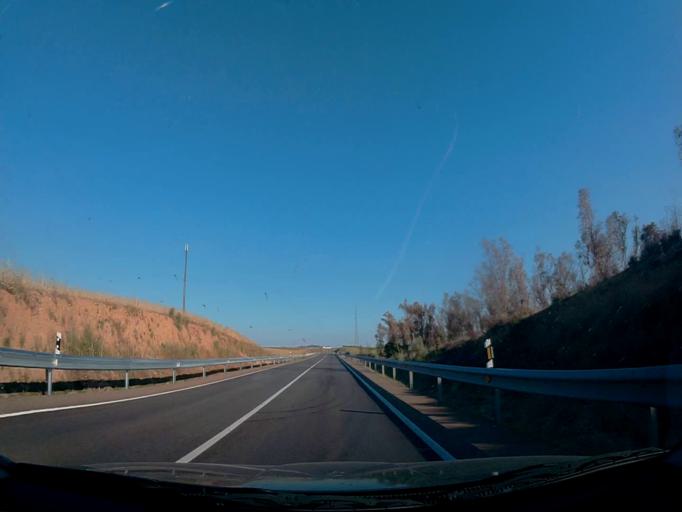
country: ES
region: Castille-La Mancha
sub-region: Province of Toledo
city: Hormigos
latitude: 40.1160
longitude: -4.4049
